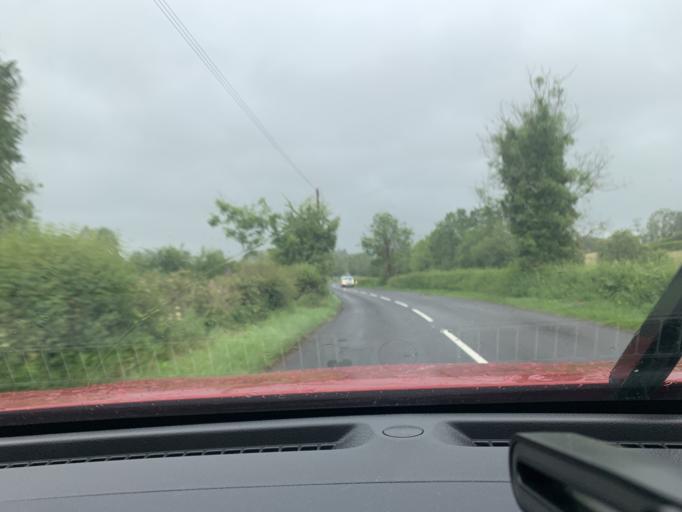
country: GB
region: Northern Ireland
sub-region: Fermanagh District
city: Enniskillen
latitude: 54.3062
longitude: -7.6862
